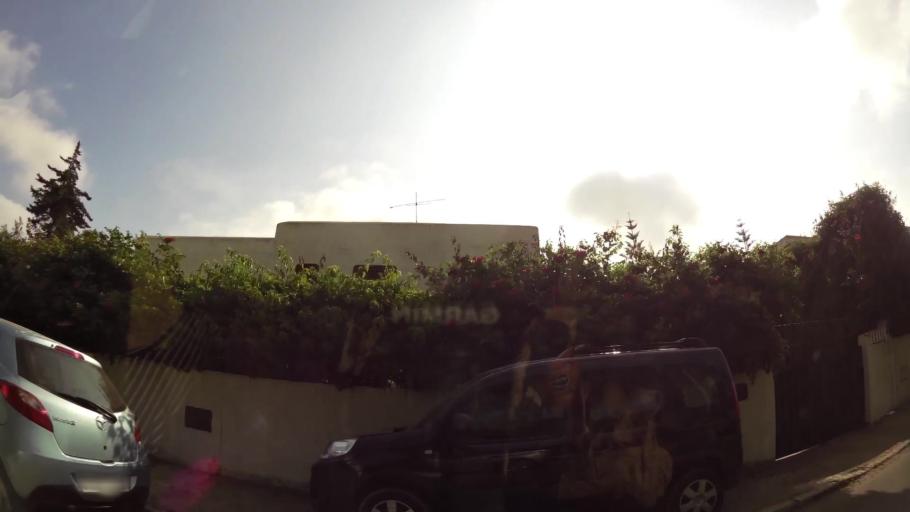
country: MA
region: Rabat-Sale-Zemmour-Zaer
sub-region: Rabat
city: Rabat
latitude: 33.9661
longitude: -6.8445
